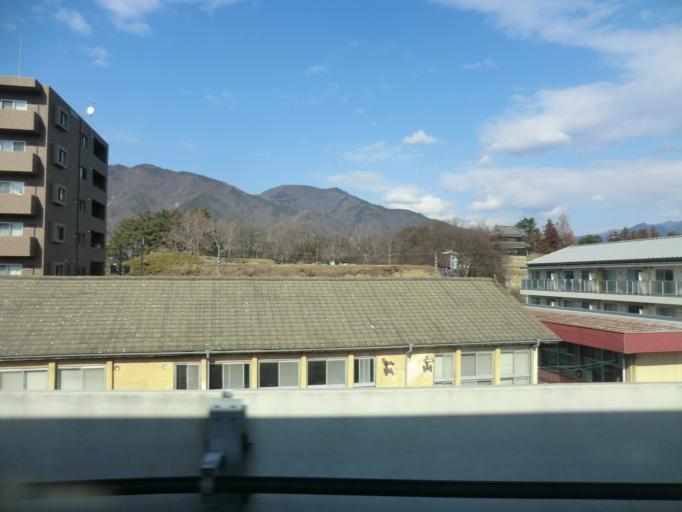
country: JP
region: Nagano
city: Ueda
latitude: 36.4025
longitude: 138.2418
